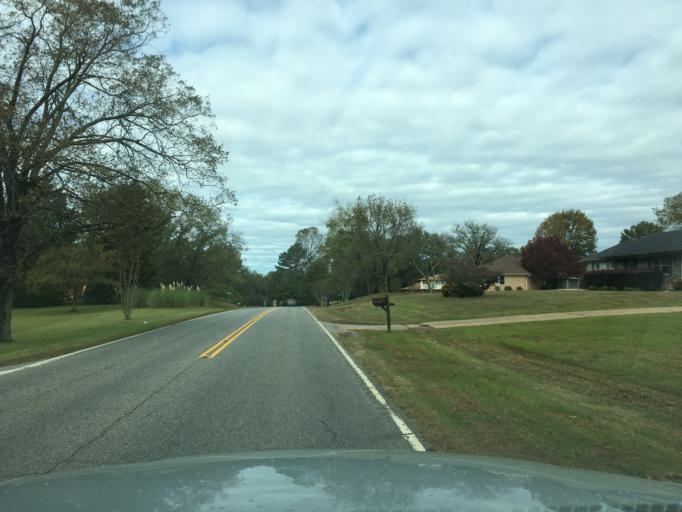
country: US
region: South Carolina
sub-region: Greenville County
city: Greer
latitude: 34.9773
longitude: -82.2098
